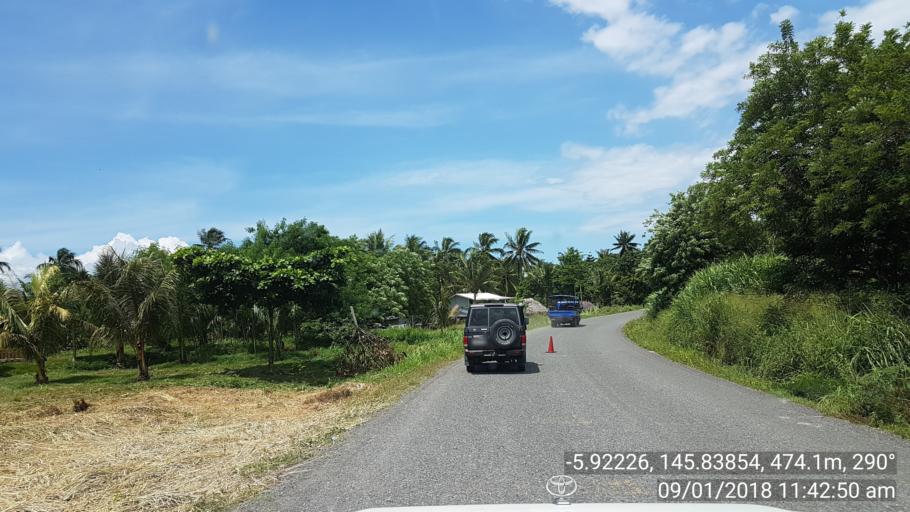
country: PG
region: Eastern Highlands
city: Kainantu
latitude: -5.9221
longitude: 145.8385
